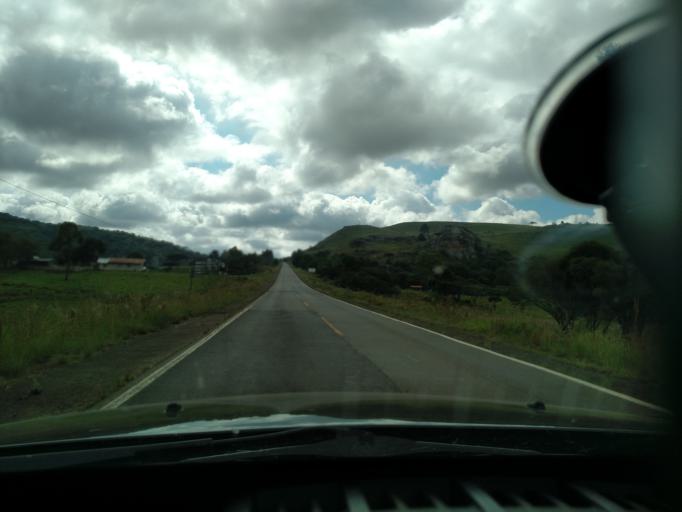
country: BR
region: Santa Catarina
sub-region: Lages
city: Lages
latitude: -27.8660
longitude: -50.2014
